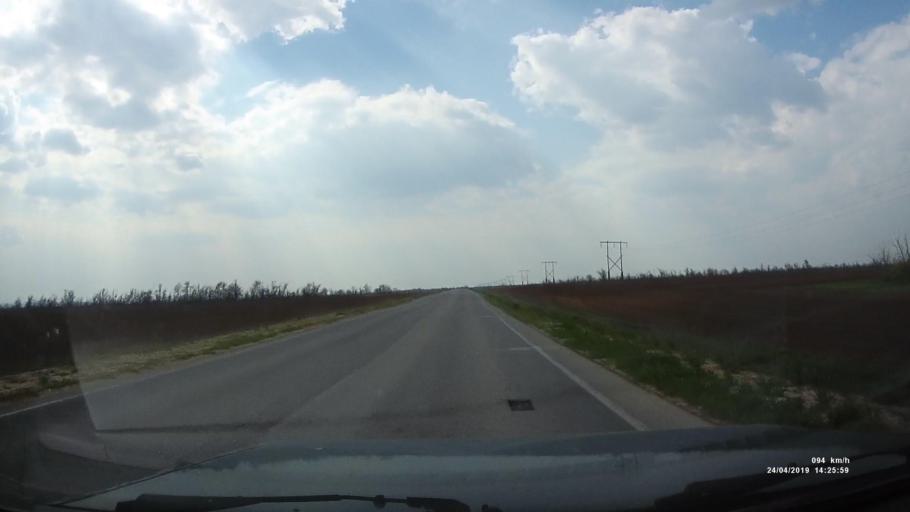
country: RU
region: Kalmykiya
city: Arshan'
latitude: 46.3324
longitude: 44.0714
